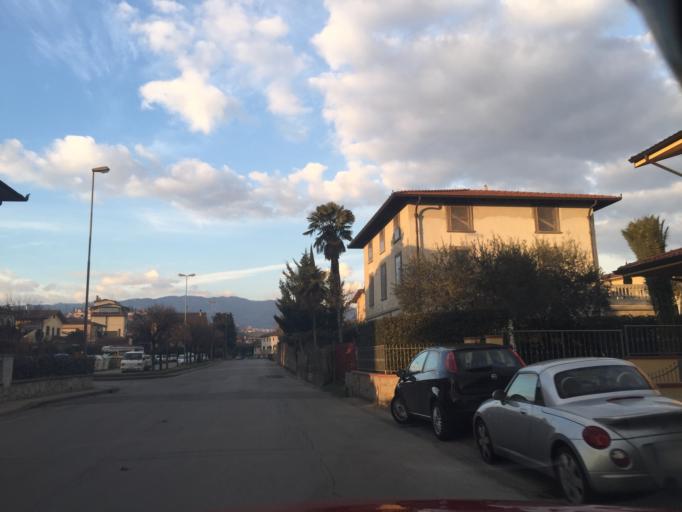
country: IT
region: Tuscany
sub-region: Provincia di Pistoia
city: Borgo a Buggiano
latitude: 43.8726
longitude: 10.7315
